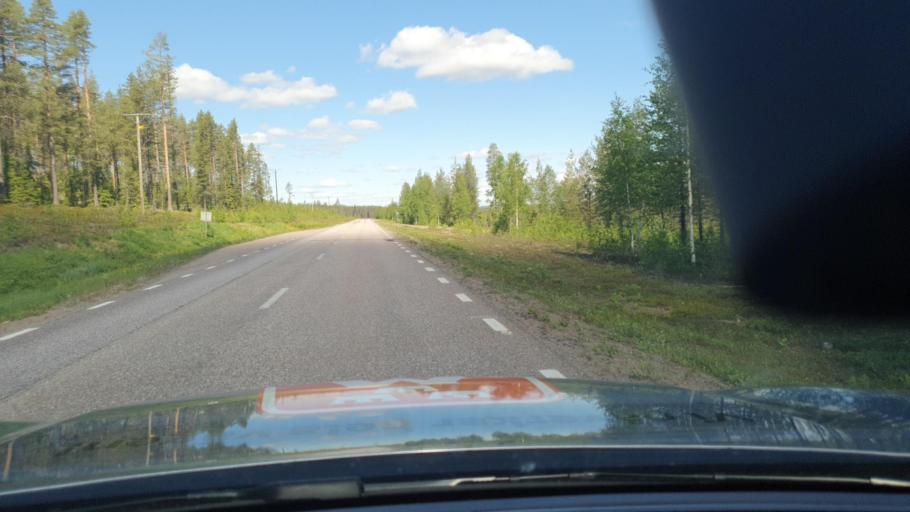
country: SE
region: Norrbotten
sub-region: Overkalix Kommun
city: OEverkalix
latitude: 67.0269
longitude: 22.5131
